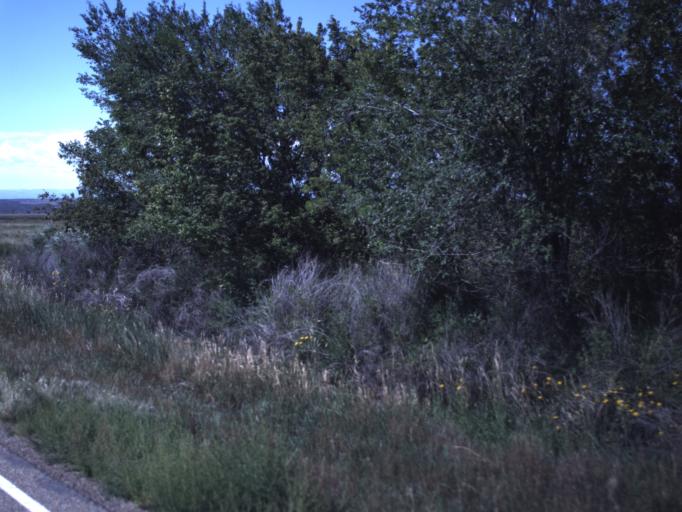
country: US
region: Utah
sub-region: Duchesne County
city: Duchesne
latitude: 40.3516
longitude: -110.2752
